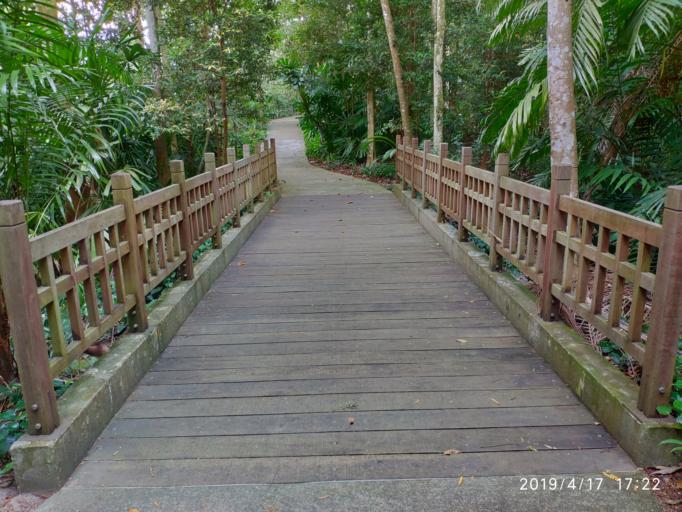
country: SG
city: Singapore
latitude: 1.3488
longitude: 103.7754
